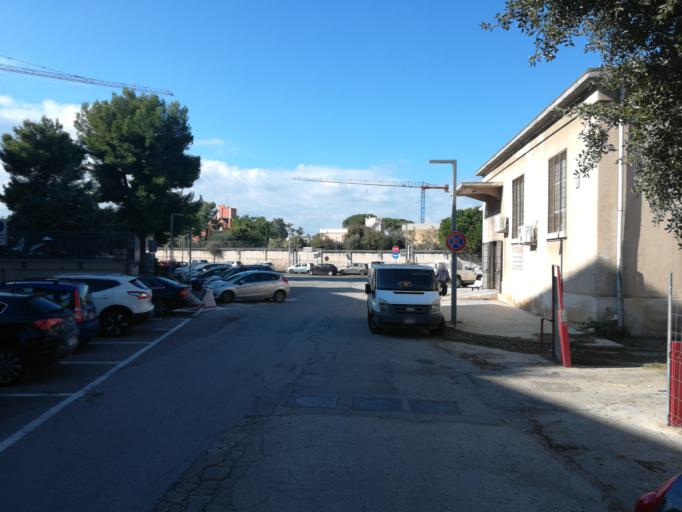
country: IT
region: Apulia
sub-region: Provincia di Bari
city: Bari
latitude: 41.1107
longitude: 16.8570
